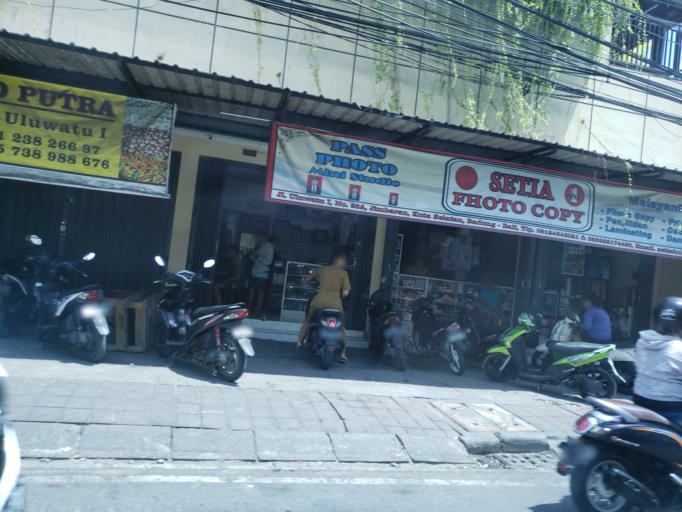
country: ID
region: Bali
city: Kelanabian
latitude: -8.7715
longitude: 115.1730
